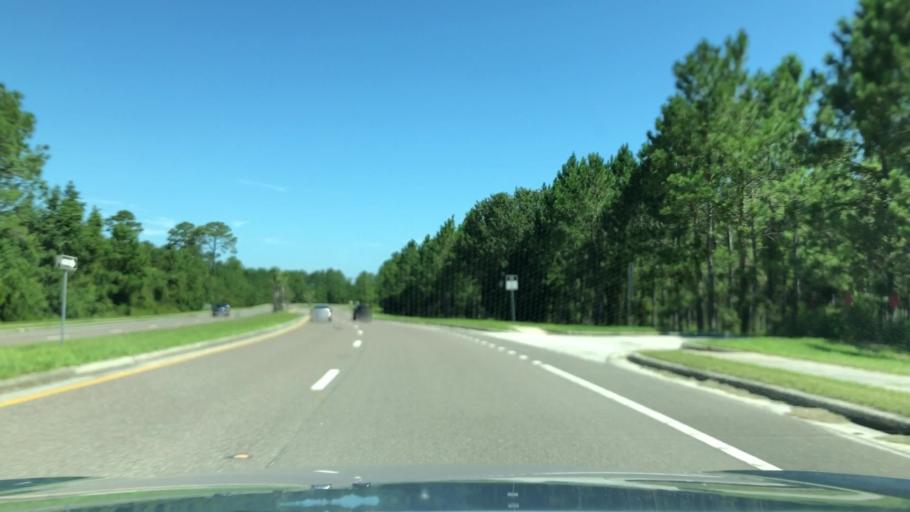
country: US
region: Florida
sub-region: Saint Johns County
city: Fruit Cove
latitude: 30.0981
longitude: -81.5383
